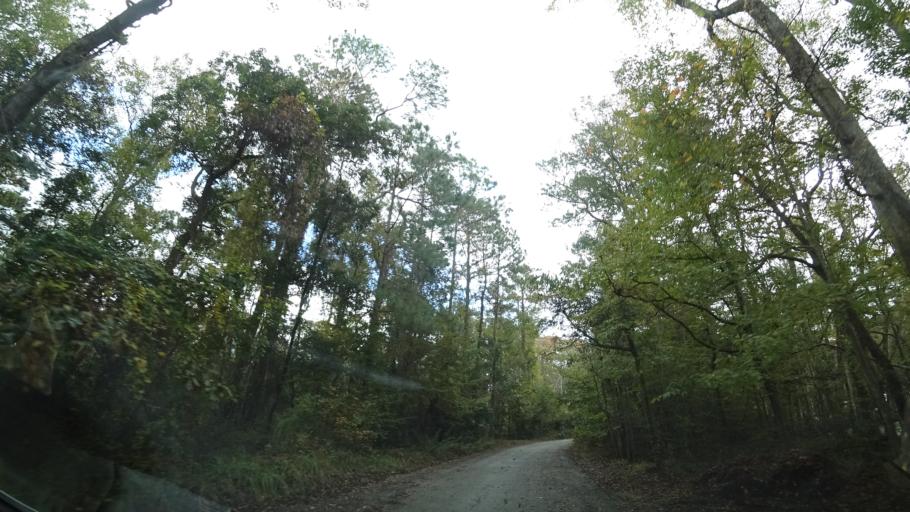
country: US
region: North Carolina
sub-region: Dare County
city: Kill Devil Hills
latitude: 35.9903
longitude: -75.6653
